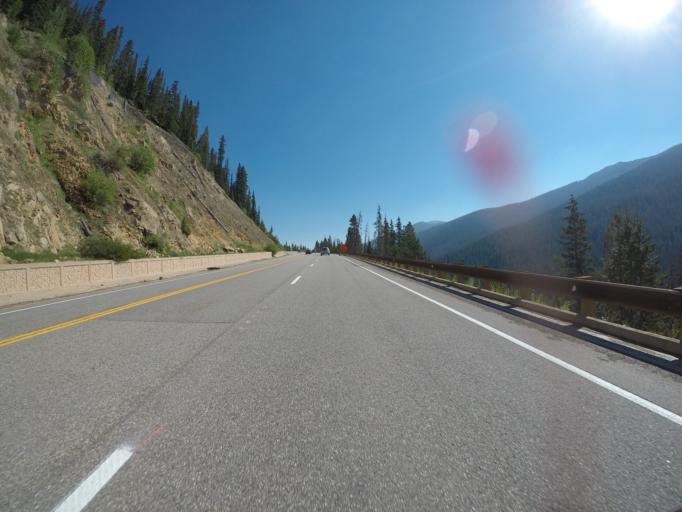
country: US
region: Colorado
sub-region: Grand County
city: Fraser
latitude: 39.8317
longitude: -105.7592
